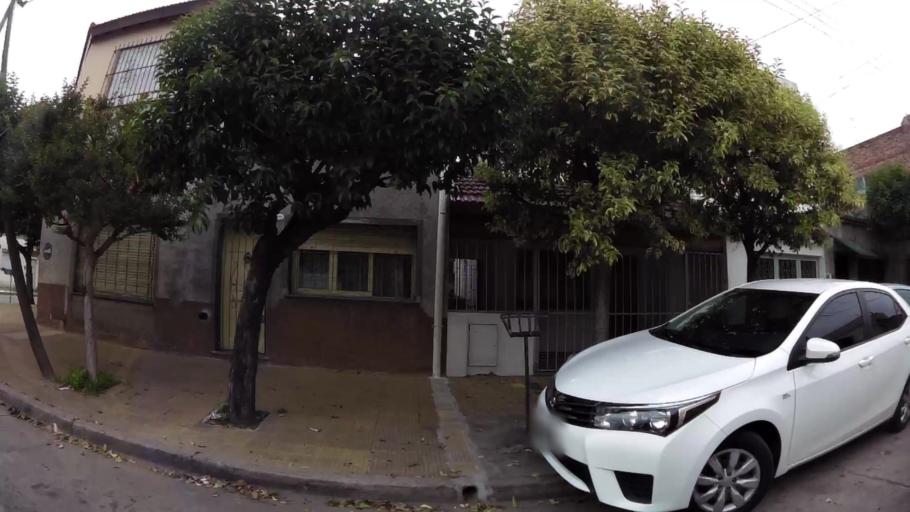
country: AR
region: Buenos Aires F.D.
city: Villa Lugano
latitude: -34.6827
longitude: -58.5080
